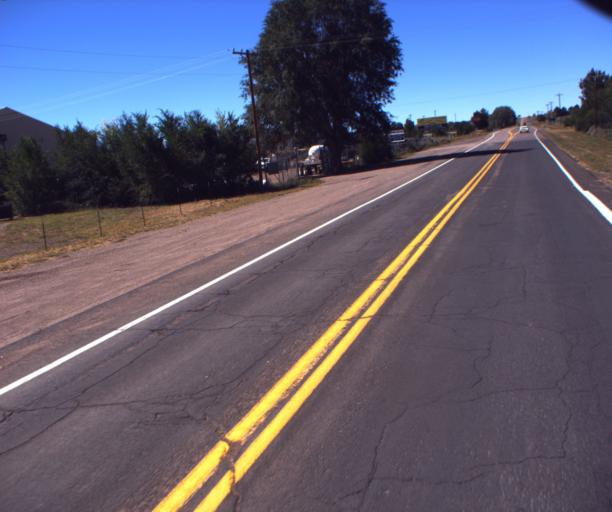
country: US
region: Arizona
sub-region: Apache County
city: Saint Johns
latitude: 34.5065
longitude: -109.3872
